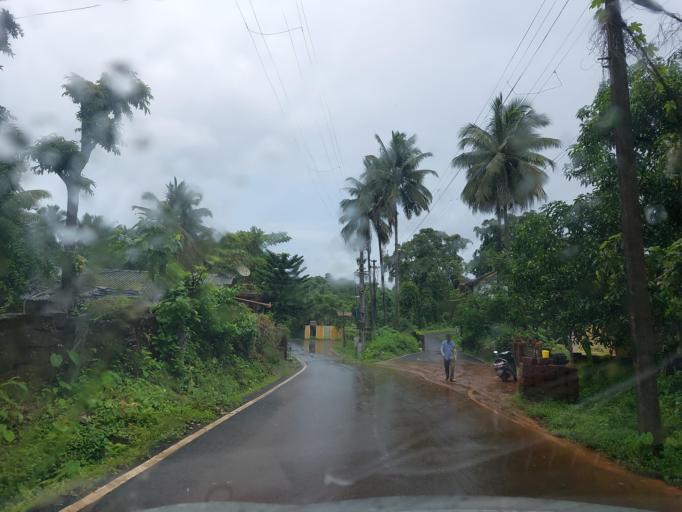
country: IN
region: Goa
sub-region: North Goa
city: Valpoy
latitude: 15.5297
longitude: 74.1314
